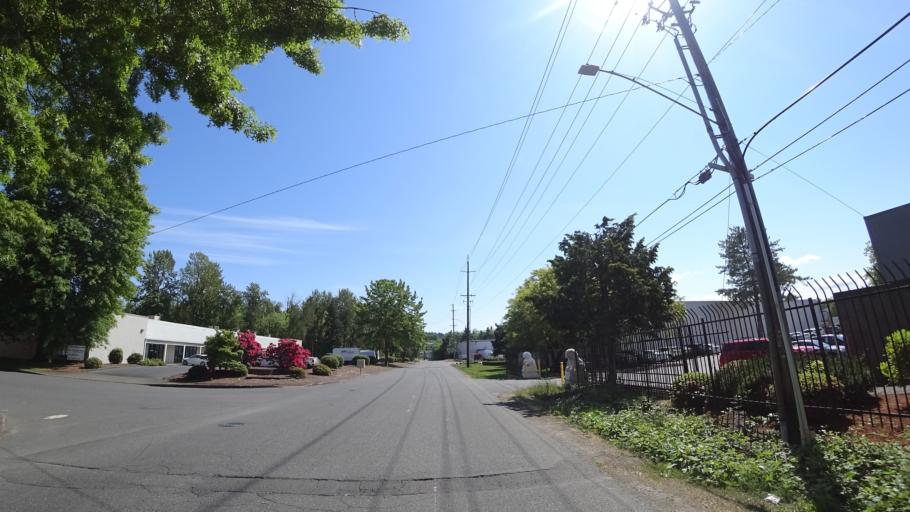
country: US
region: Oregon
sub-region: Multnomah County
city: Lents
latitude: 45.5678
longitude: -122.5677
